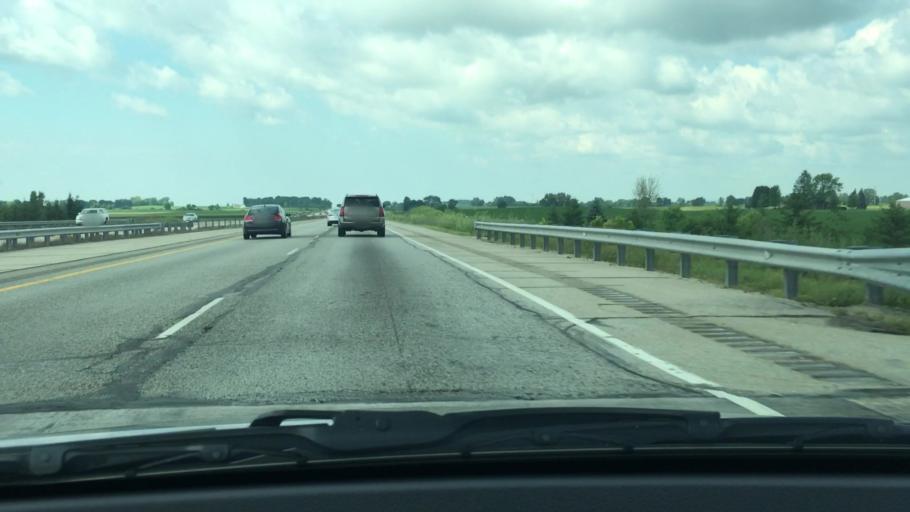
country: US
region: Wisconsin
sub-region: Dodge County
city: Lomira
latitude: 43.6608
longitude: -88.4414
